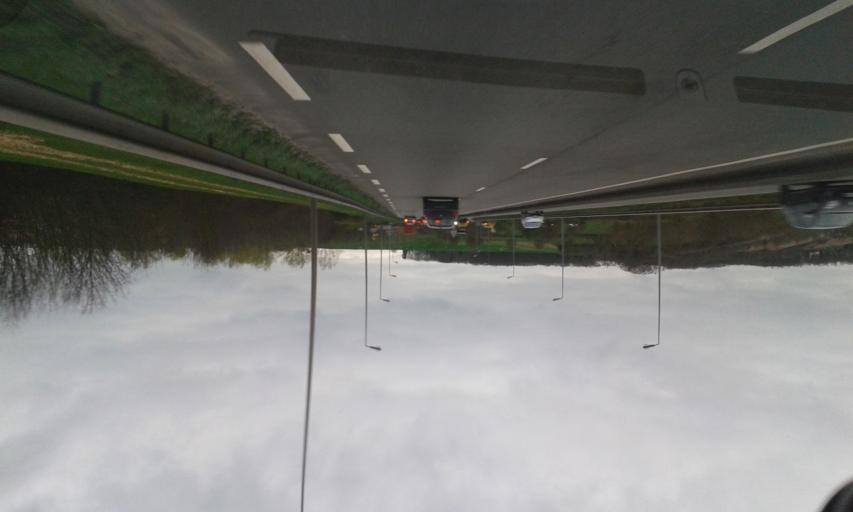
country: FR
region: Centre
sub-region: Departement d'Eure-et-Loir
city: Vernouillet
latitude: 48.7171
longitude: 1.3512
